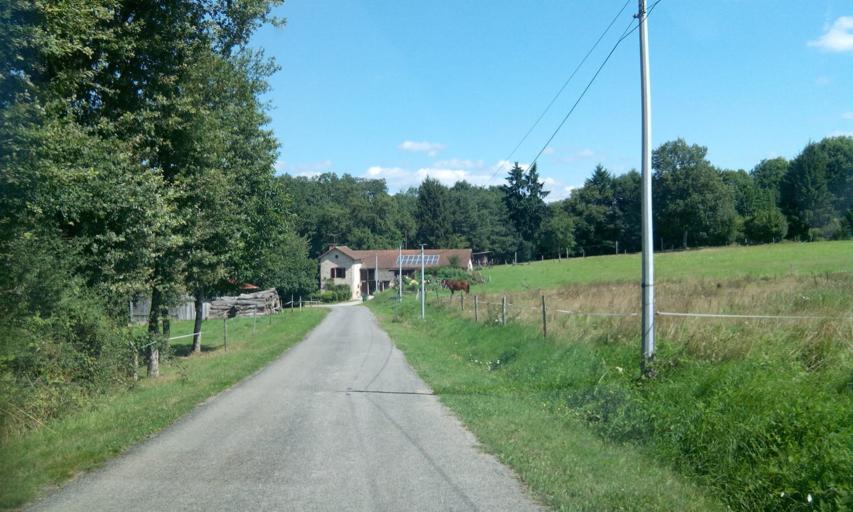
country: FR
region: Limousin
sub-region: Departement de la Haute-Vienne
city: Saint-Leonard-de-Noblat
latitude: 45.8144
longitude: 1.4767
